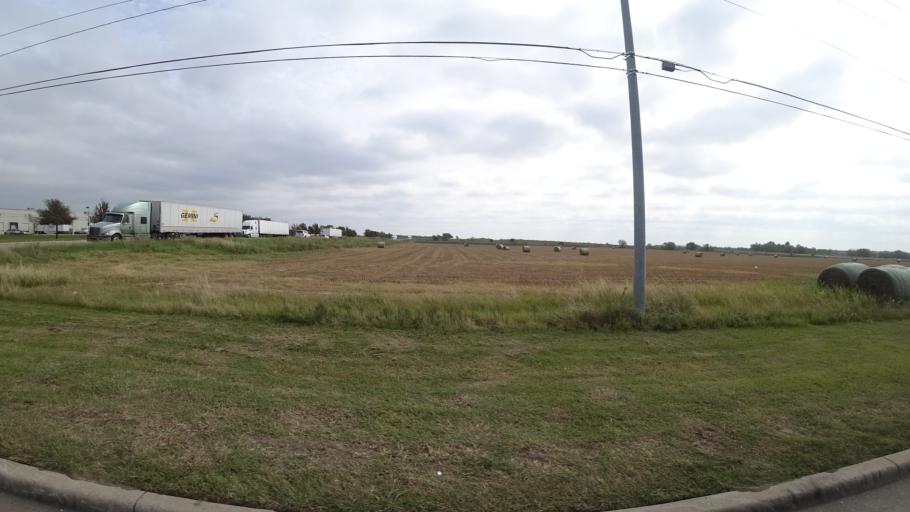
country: US
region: Texas
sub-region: Travis County
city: Manor
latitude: 30.3713
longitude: -97.6123
